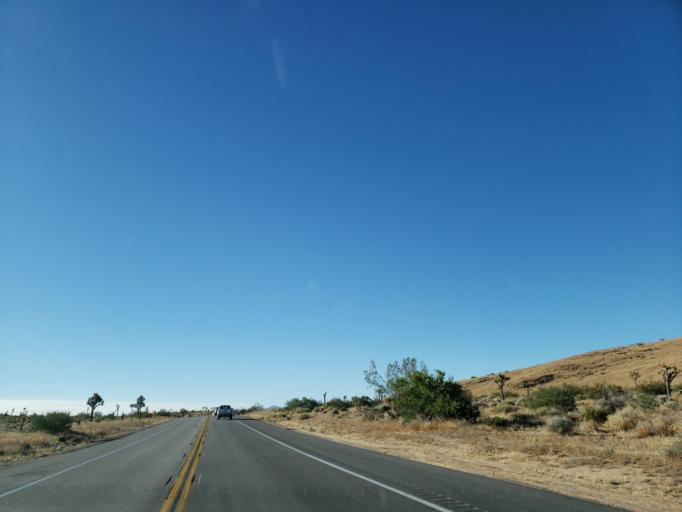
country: US
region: California
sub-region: San Bernardino County
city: Yucca Valley
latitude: 34.1890
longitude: -116.4345
